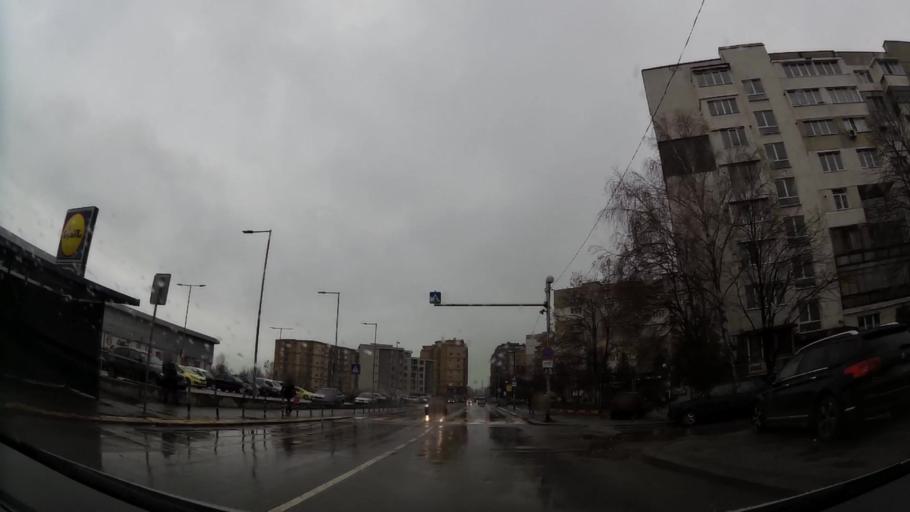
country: BG
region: Sofia-Capital
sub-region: Stolichna Obshtina
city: Sofia
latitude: 42.6286
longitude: 23.3830
